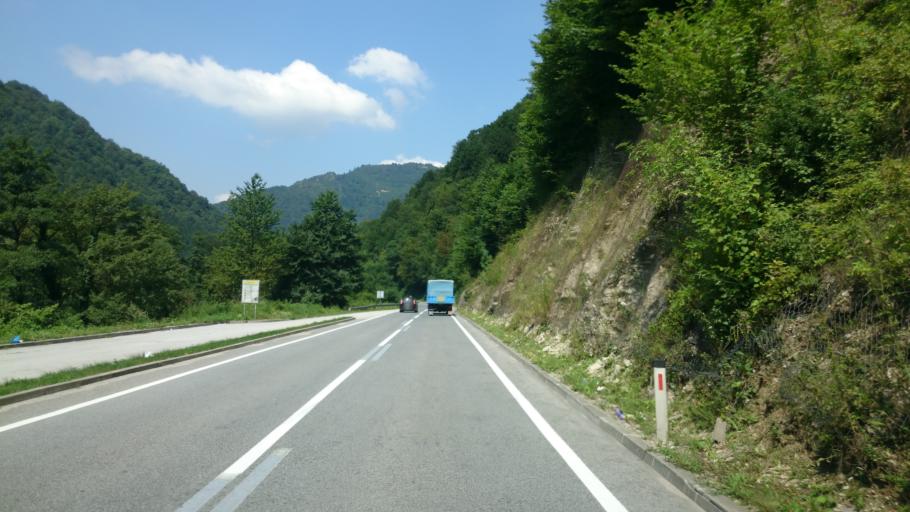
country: BA
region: Federation of Bosnia and Herzegovina
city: Donji Vakuf
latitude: 44.2190
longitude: 17.3134
